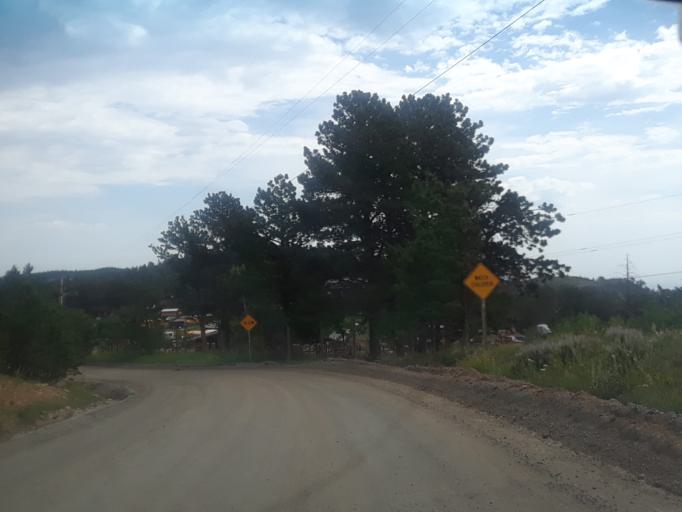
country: US
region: Colorado
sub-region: Boulder County
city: Nederland
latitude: 40.0583
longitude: -105.4192
